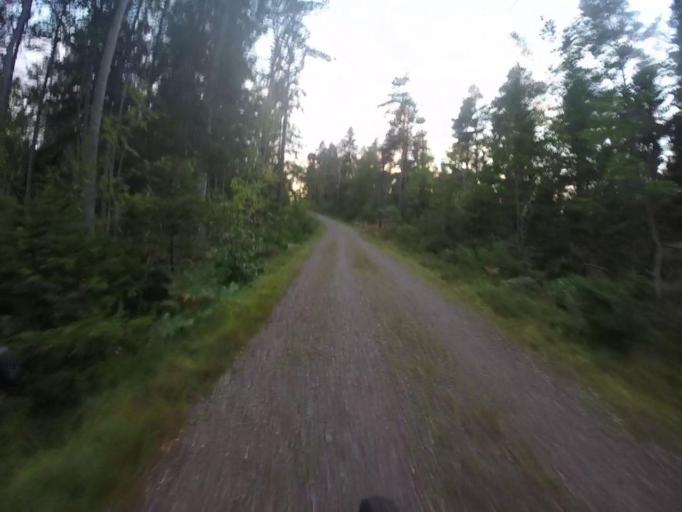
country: SE
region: Vaestra Goetaland
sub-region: Trollhattan
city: Trollhattan
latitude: 58.2978
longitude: 12.2561
